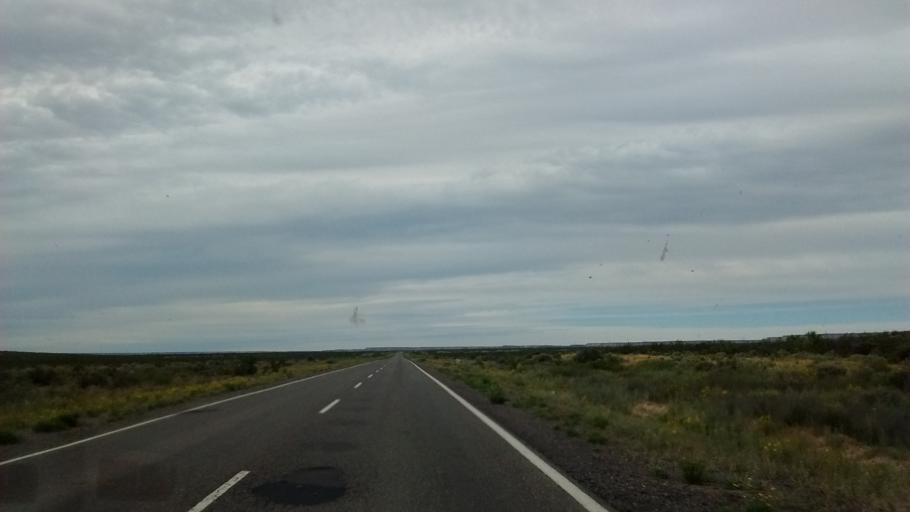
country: AR
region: Rio Negro
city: Catriel
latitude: -38.1052
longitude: -67.9288
